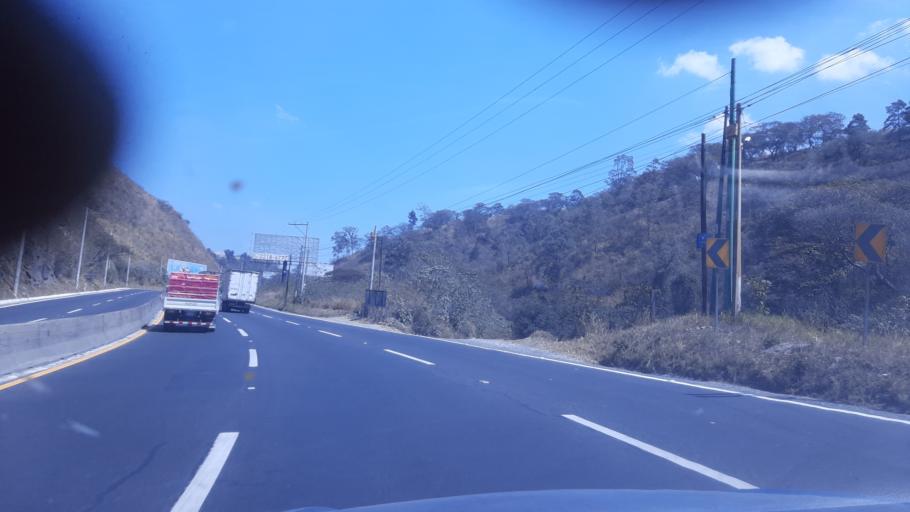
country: GT
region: Guatemala
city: Amatitlan
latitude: 14.5016
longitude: -90.6274
